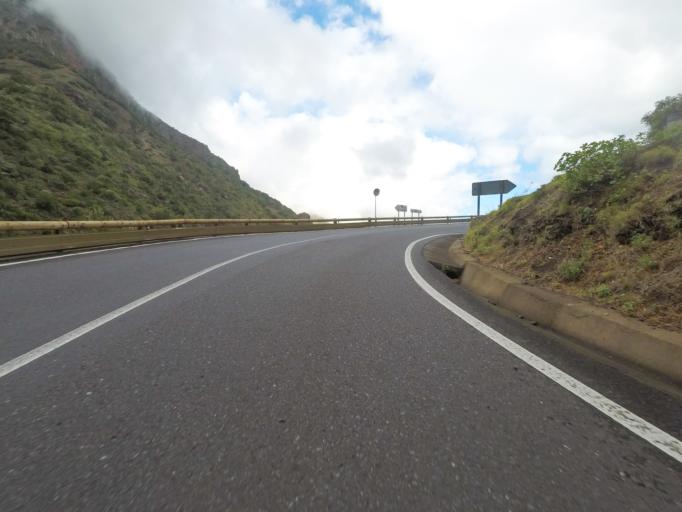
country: ES
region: Canary Islands
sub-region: Provincia de Santa Cruz de Tenerife
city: Hermigua
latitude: 28.1345
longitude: -17.2002
